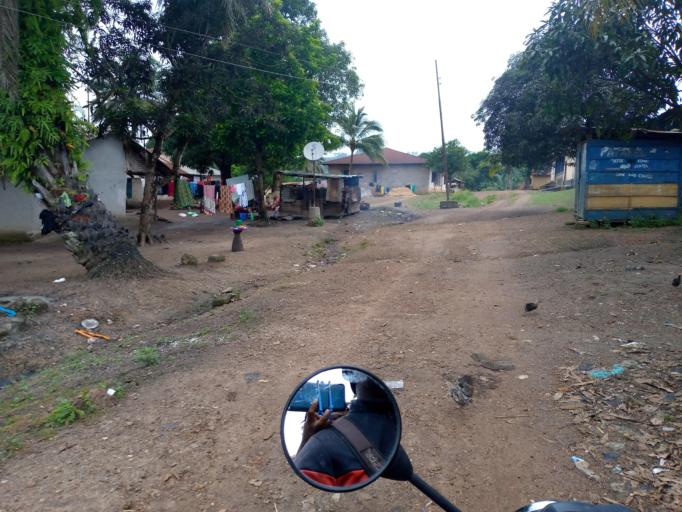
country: SL
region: Eastern Province
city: Kenema
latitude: 7.8644
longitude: -11.1913
